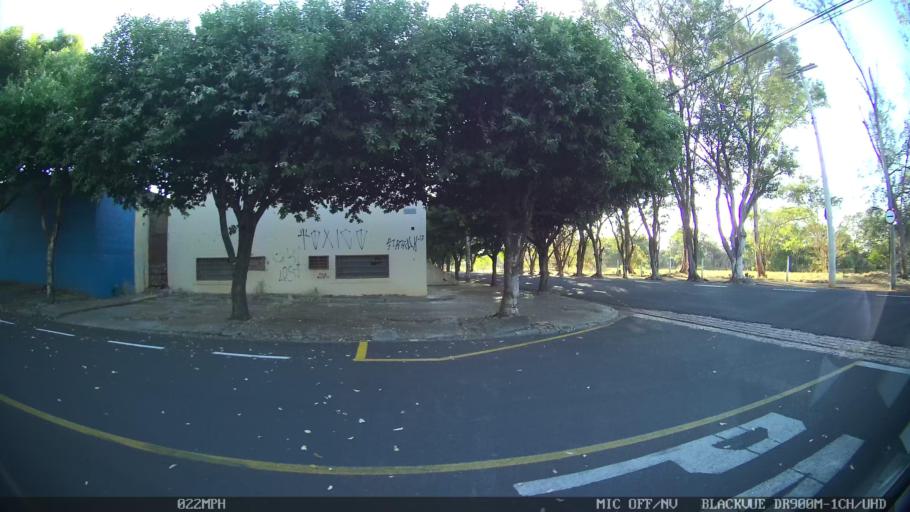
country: BR
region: Sao Paulo
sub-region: Sao Jose Do Rio Preto
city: Sao Jose do Rio Preto
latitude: -20.8243
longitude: -49.3718
